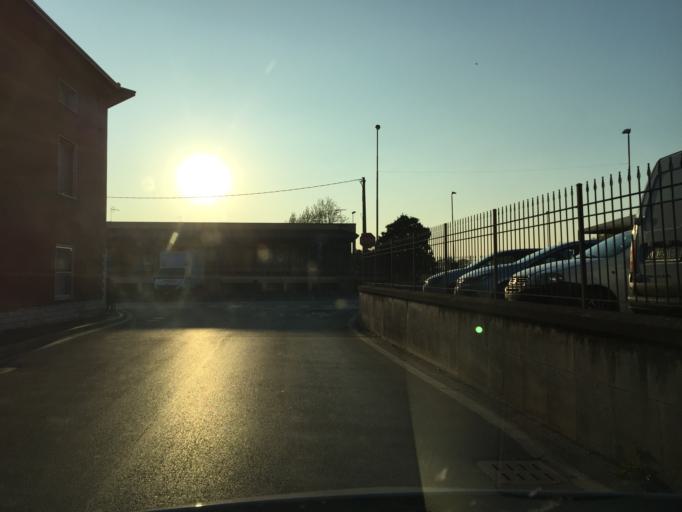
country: IT
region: Lombardy
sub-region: Provincia di Brescia
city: Pralboino
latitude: 45.2703
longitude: 10.2177
